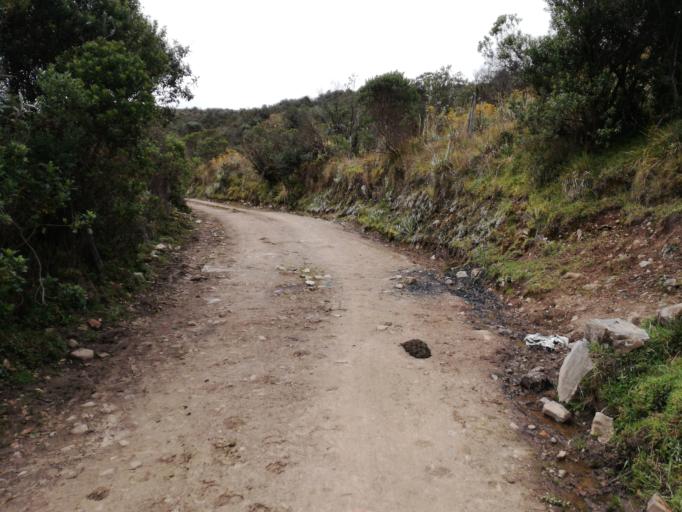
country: CO
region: Boyaca
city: Socha Viejo
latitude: 5.9000
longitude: -72.6801
